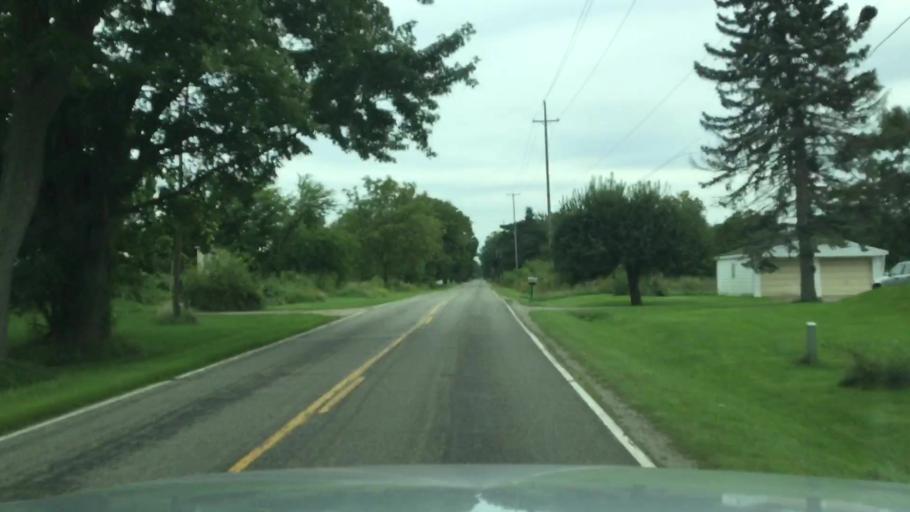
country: US
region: Michigan
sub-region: Shiawassee County
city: Durand
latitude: 42.9516
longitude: -83.9418
